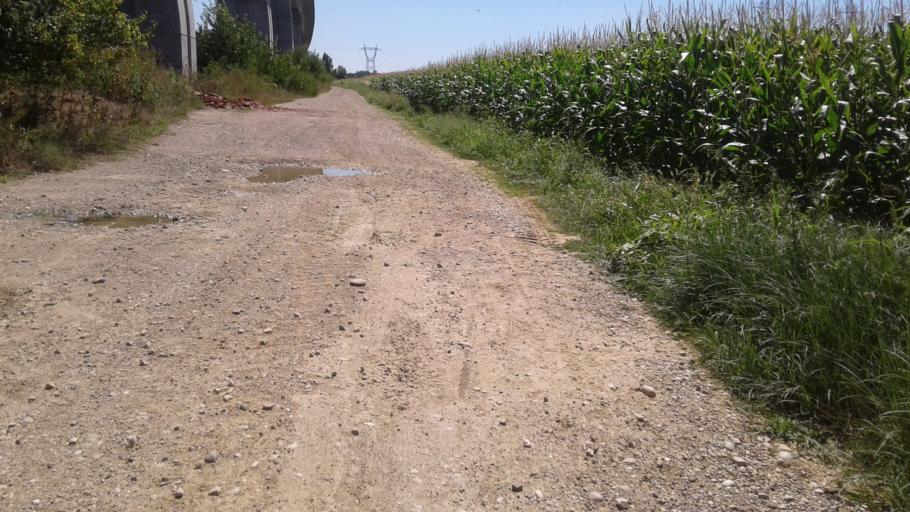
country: FR
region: Rhone-Alpes
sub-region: Departement de l'Ain
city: Beynost
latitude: 45.8338
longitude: 5.0218
